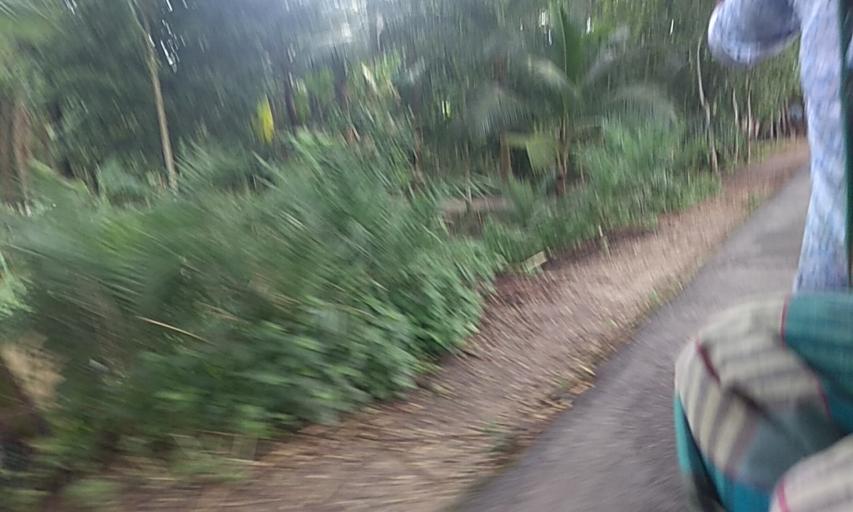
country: BD
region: Dhaka
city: Dohar
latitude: 23.4756
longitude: 90.0540
